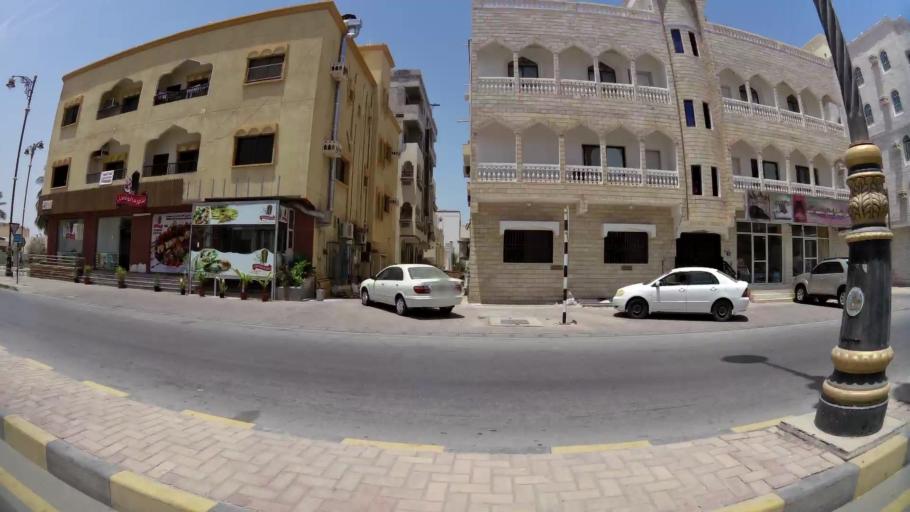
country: OM
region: Zufar
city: Salalah
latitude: 17.0213
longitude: 54.0844
